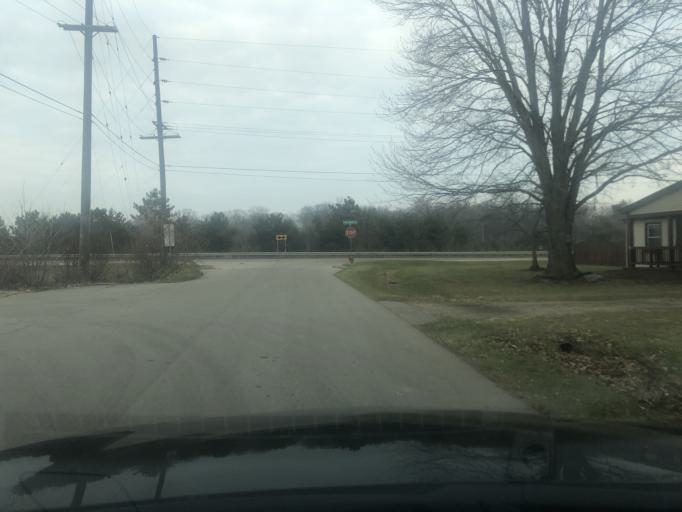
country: US
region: Michigan
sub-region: Wayne County
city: Belleville
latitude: 42.2186
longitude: -83.4812
